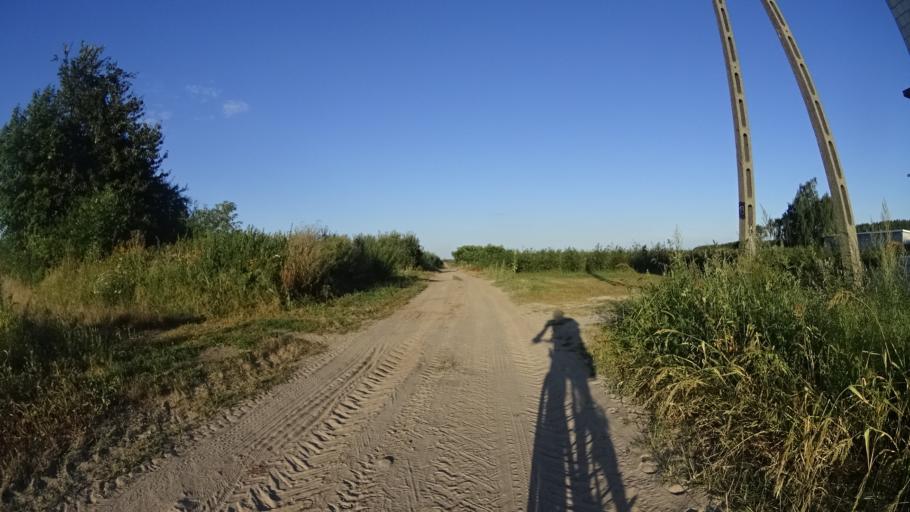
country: PL
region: Masovian Voivodeship
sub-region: Powiat bialobrzeski
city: Wysmierzyce
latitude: 51.6582
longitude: 20.7842
